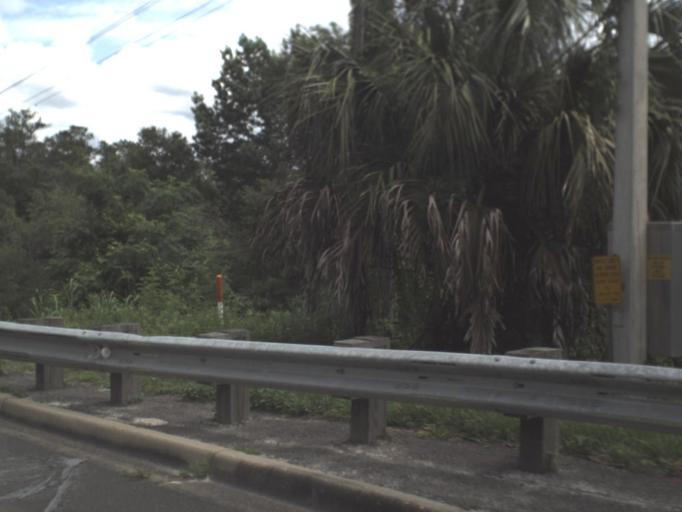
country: US
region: Georgia
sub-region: Charlton County
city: Folkston
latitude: 30.7760
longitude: -81.9789
